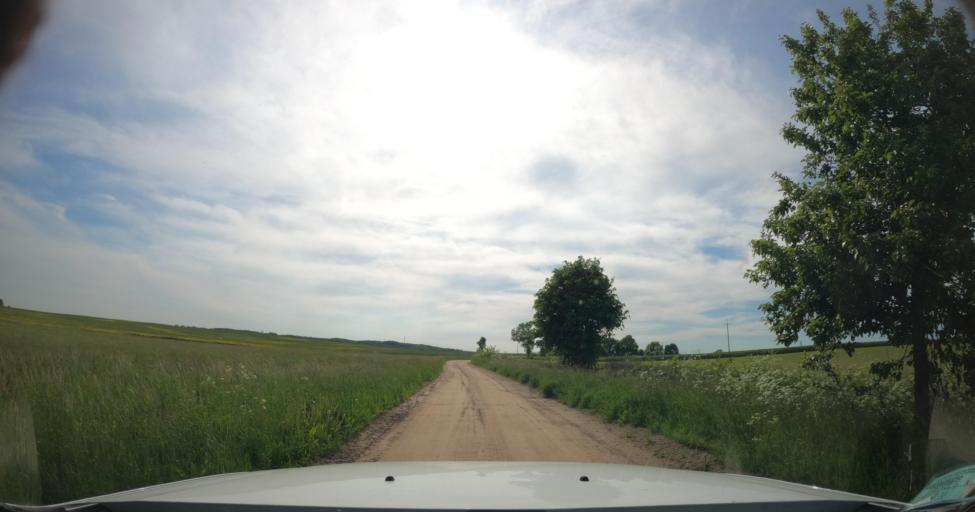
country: PL
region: Warmian-Masurian Voivodeship
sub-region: Powiat ostrodzki
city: Milakowo
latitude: 54.0154
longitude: 20.0142
